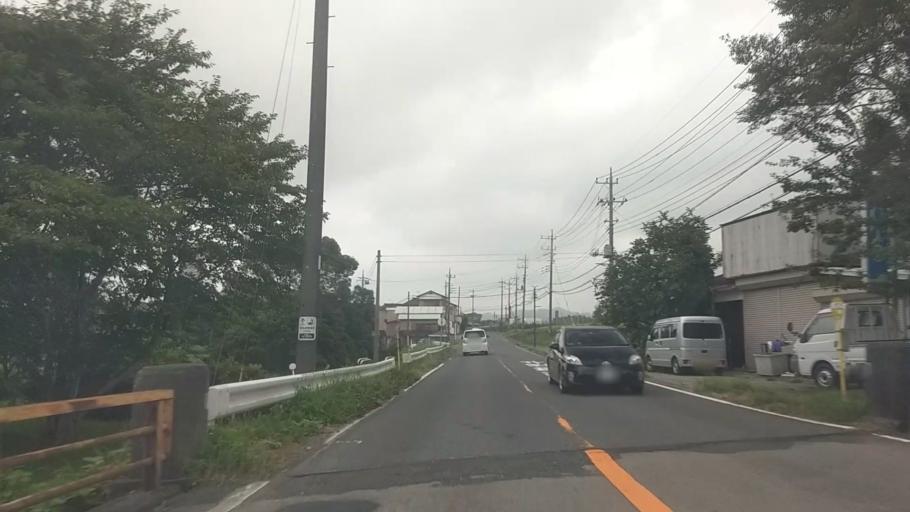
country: JP
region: Chiba
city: Kawaguchi
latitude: 35.1141
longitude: 140.0808
